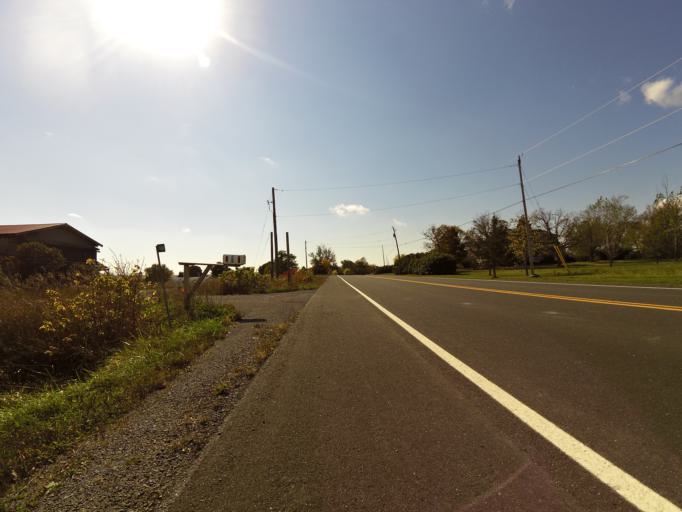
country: CA
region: Ontario
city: Deseronto
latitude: 44.0924
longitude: -76.9491
